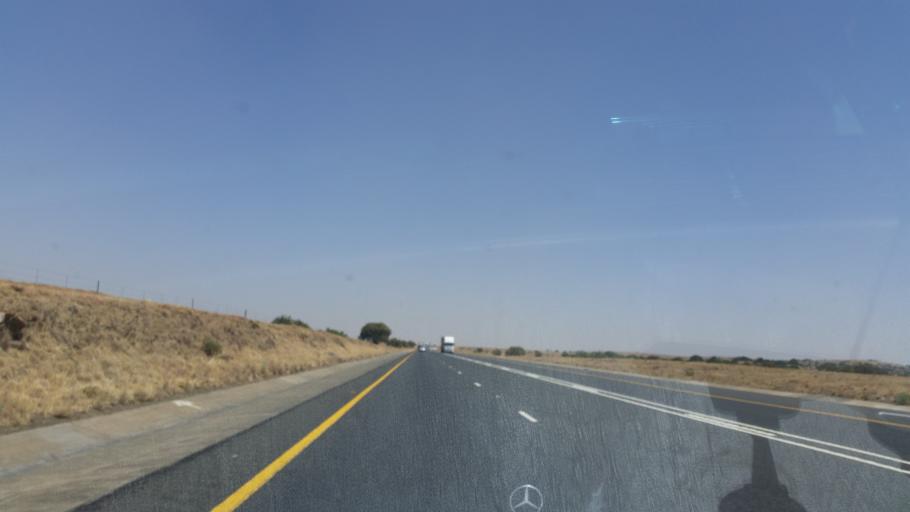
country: ZA
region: Orange Free State
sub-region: Lejweleputswa District Municipality
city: Winburg
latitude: -28.7015
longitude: 26.7977
